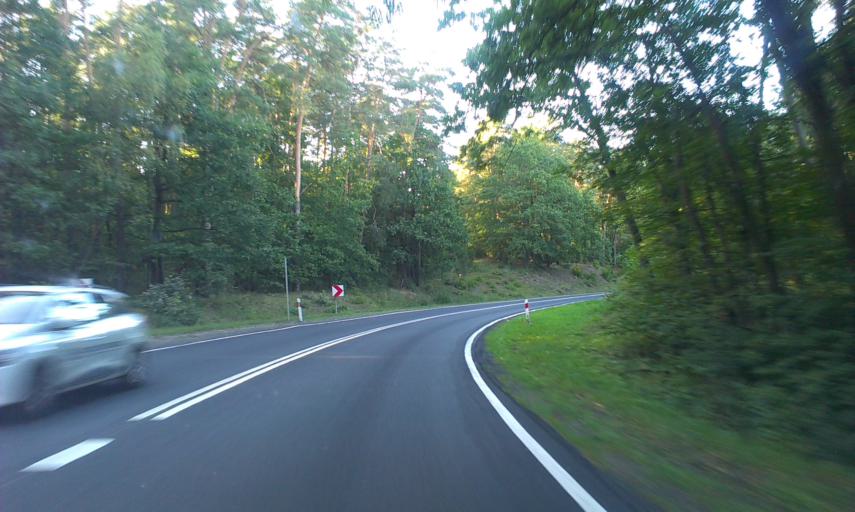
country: PL
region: Kujawsko-Pomorskie
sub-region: Powiat tucholski
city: Tuchola
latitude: 53.5551
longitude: 17.9015
